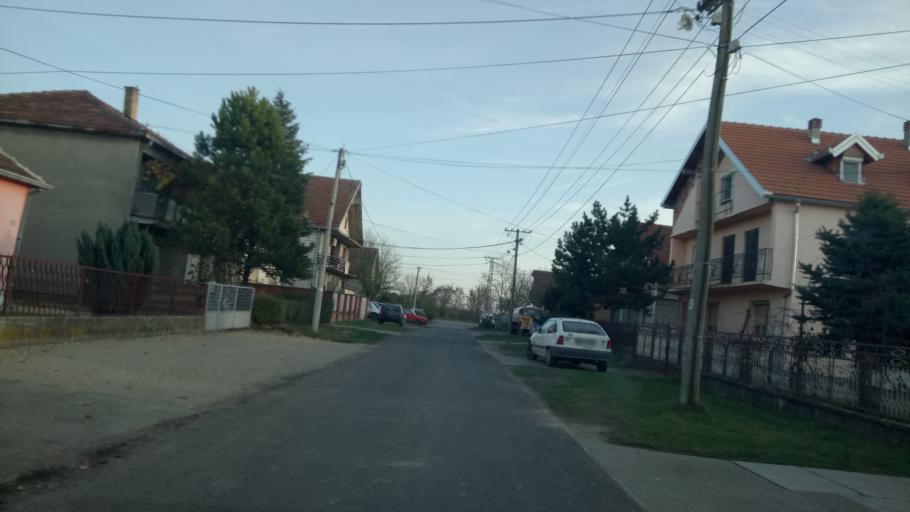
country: RS
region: Autonomna Pokrajina Vojvodina
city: Nova Pazova
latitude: 44.9359
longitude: 20.2253
